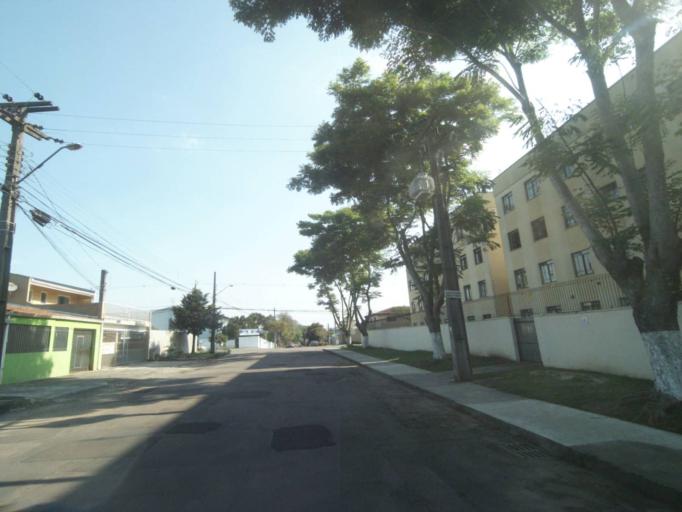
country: BR
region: Parana
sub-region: Curitiba
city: Curitiba
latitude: -25.4894
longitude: -49.3257
